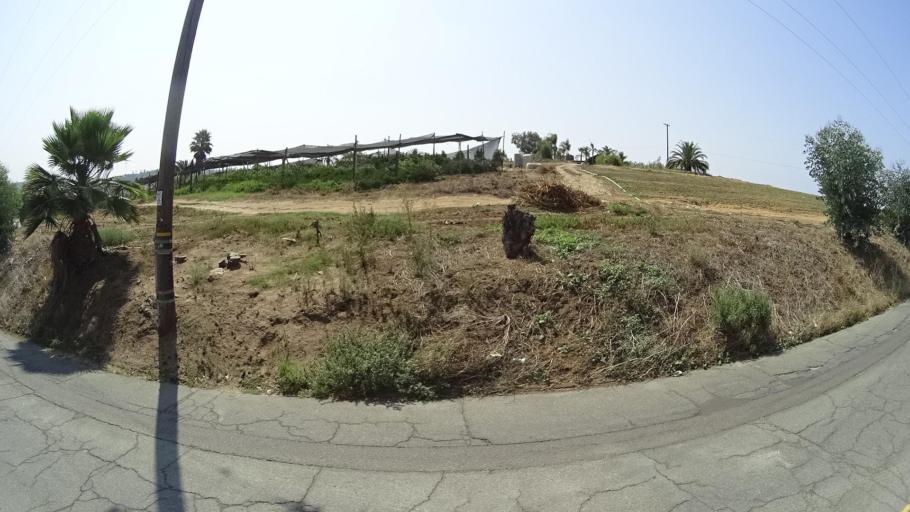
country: US
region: California
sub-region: San Diego County
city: Bonsall
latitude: 33.2685
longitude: -117.2418
